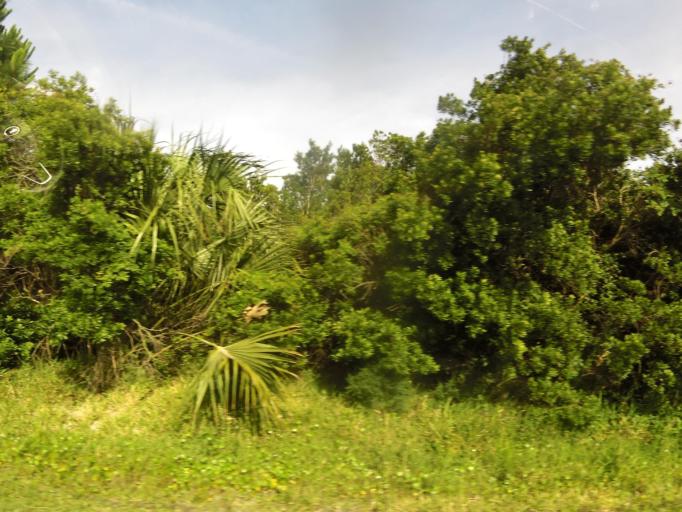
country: US
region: Florida
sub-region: Nassau County
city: Fernandina Beach
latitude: 30.5174
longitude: -81.4704
